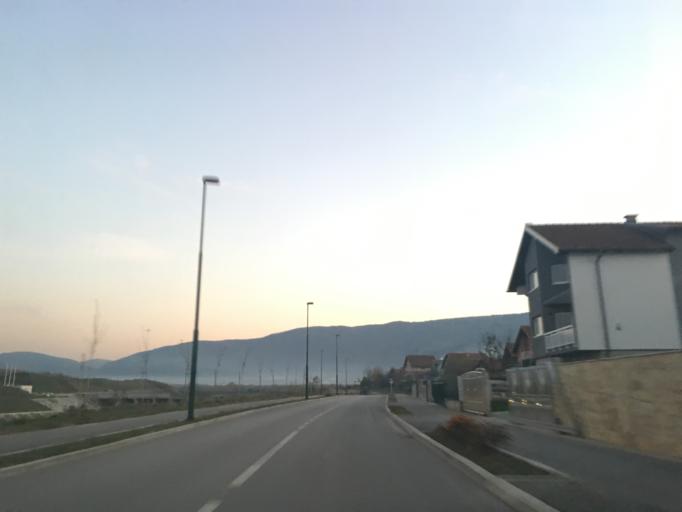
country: BA
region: Federation of Bosnia and Herzegovina
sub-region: Kanton Sarajevo
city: Sarajevo
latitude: 43.8134
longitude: 18.3213
